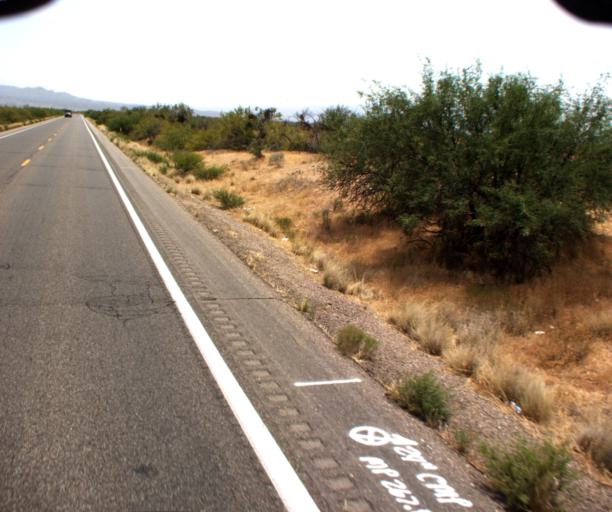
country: US
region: Arizona
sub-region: Gila County
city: Peridot
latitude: 33.3134
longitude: -110.5142
